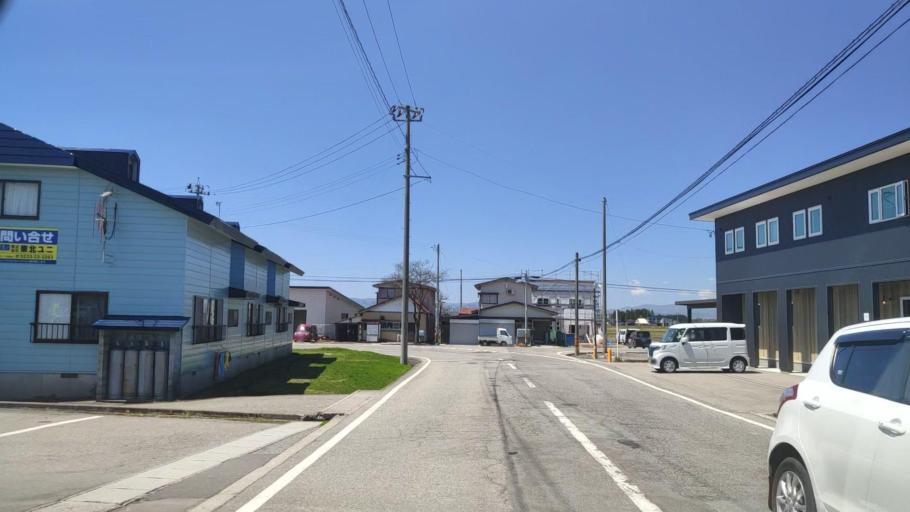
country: JP
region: Yamagata
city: Shinjo
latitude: 38.7748
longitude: 140.3102
